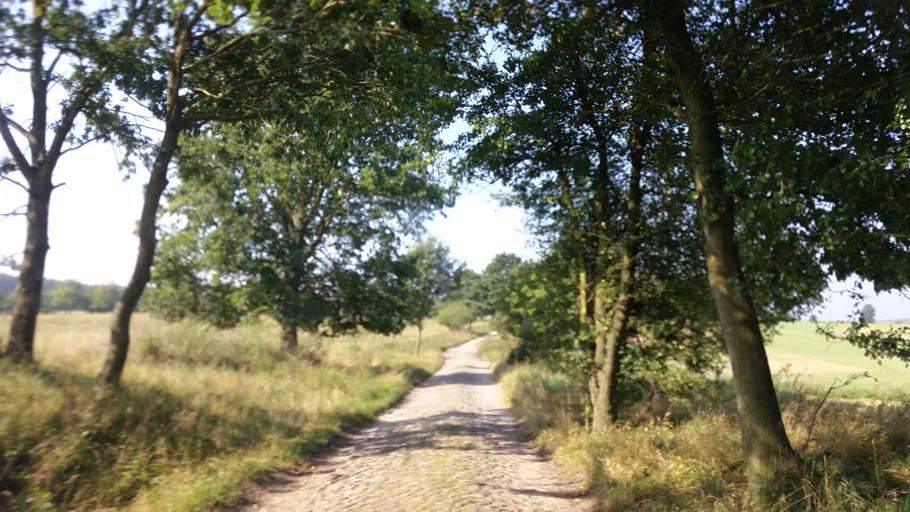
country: PL
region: West Pomeranian Voivodeship
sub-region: Powiat choszczenski
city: Pelczyce
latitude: 52.9773
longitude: 15.3467
